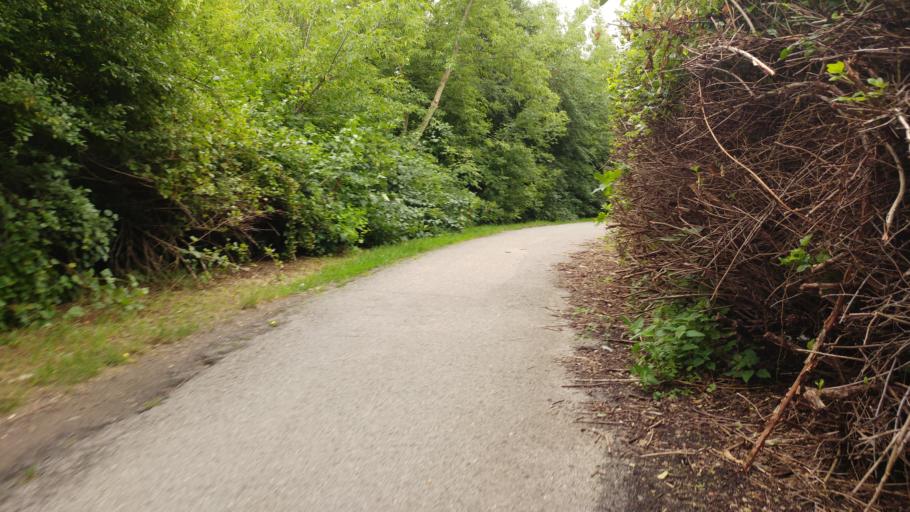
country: CZ
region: Central Bohemia
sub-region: Okres Praha-Zapad
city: Pruhonice
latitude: 50.0386
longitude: 14.5349
